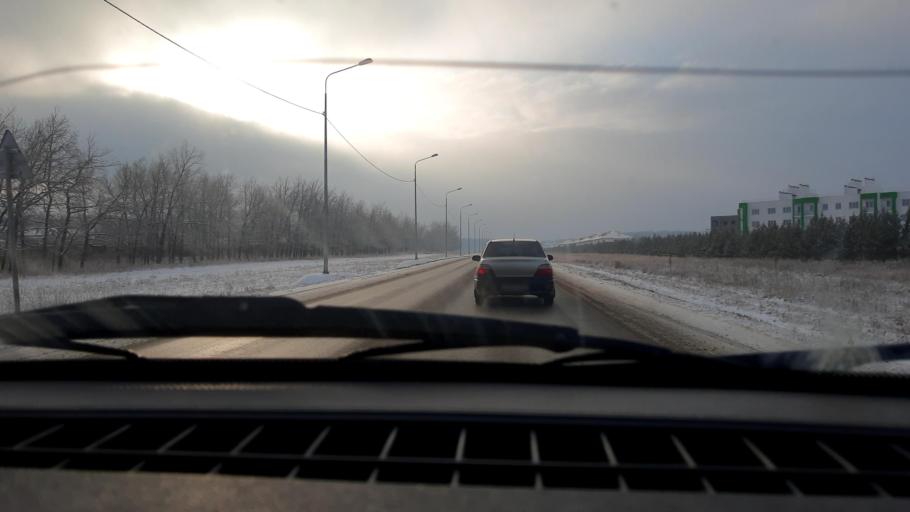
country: RU
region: Bashkortostan
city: Avdon
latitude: 54.4842
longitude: 55.8905
